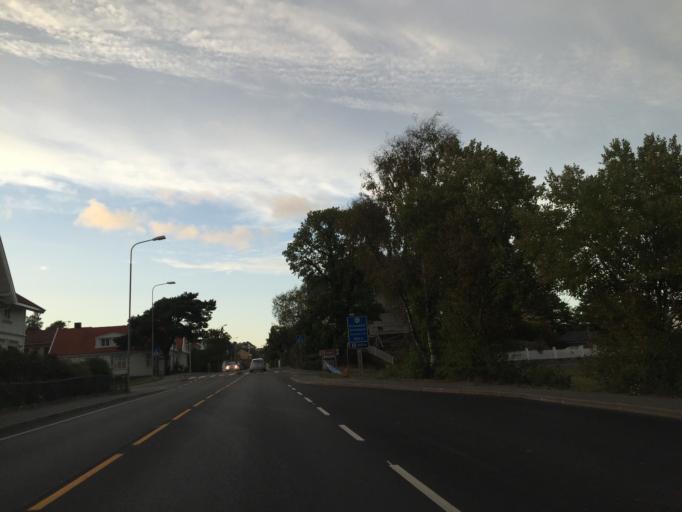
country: NO
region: Ostfold
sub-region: Fredrikstad
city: Fredrikstad
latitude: 59.2032
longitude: 10.9385
